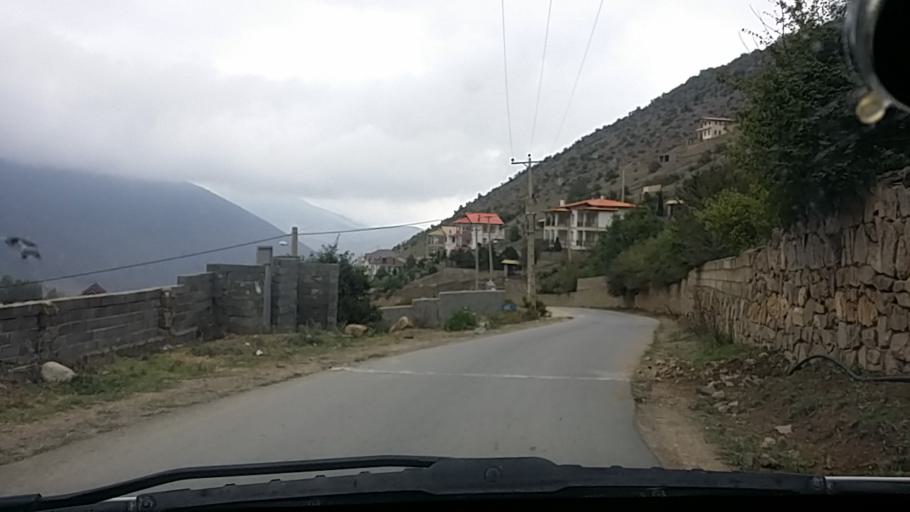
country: IR
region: Mazandaran
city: `Abbasabad
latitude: 36.4731
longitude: 51.1401
